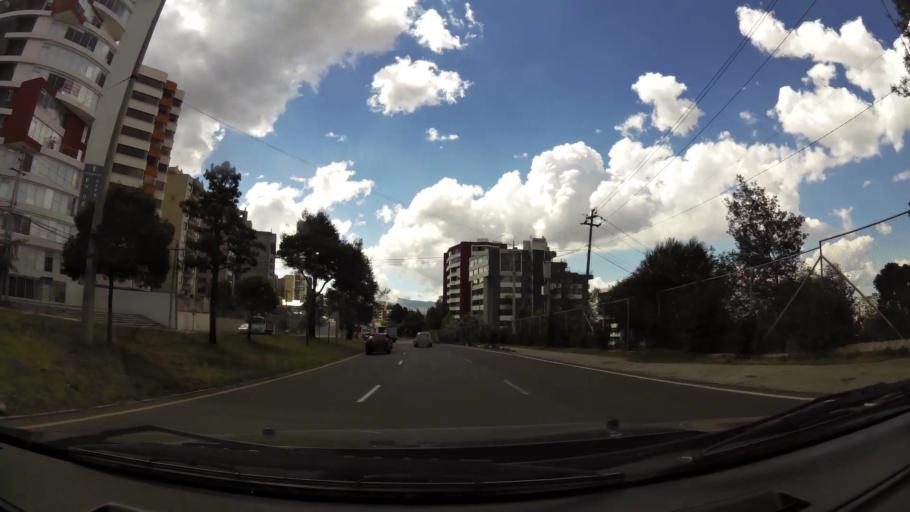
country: EC
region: Pichincha
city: Quito
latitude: -0.1634
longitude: -78.4953
